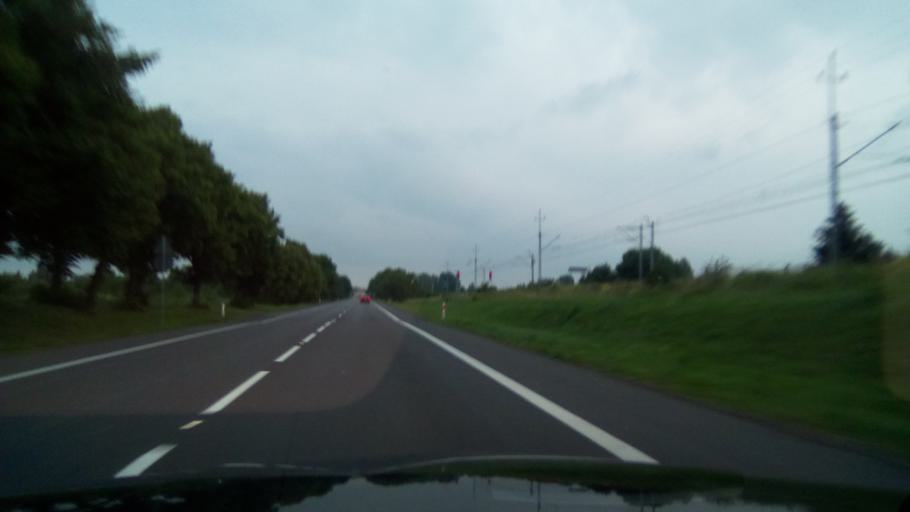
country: PL
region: Greater Poland Voivodeship
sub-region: Powiat poznanski
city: Pobiedziska
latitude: 52.4764
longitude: 17.2576
